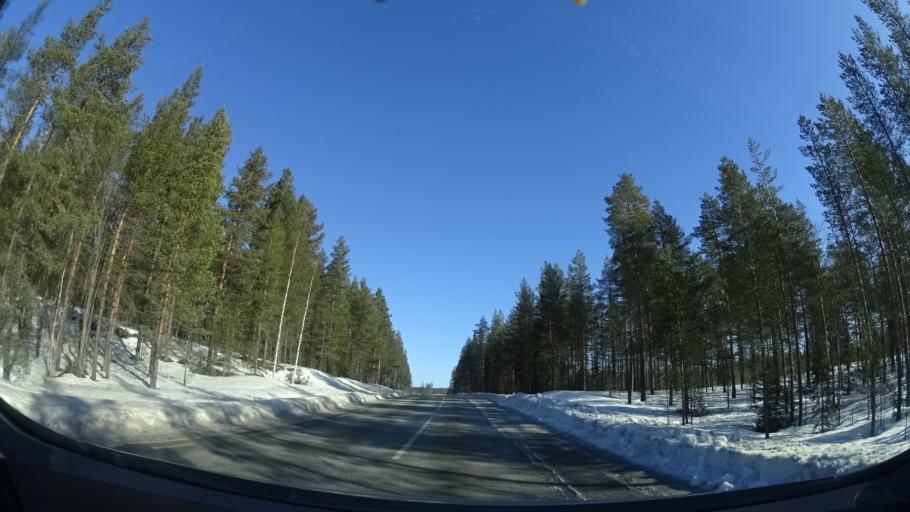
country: SE
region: Vaesterbotten
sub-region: Skelleftea Kommun
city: Langsele
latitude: 65.0778
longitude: 20.0660
